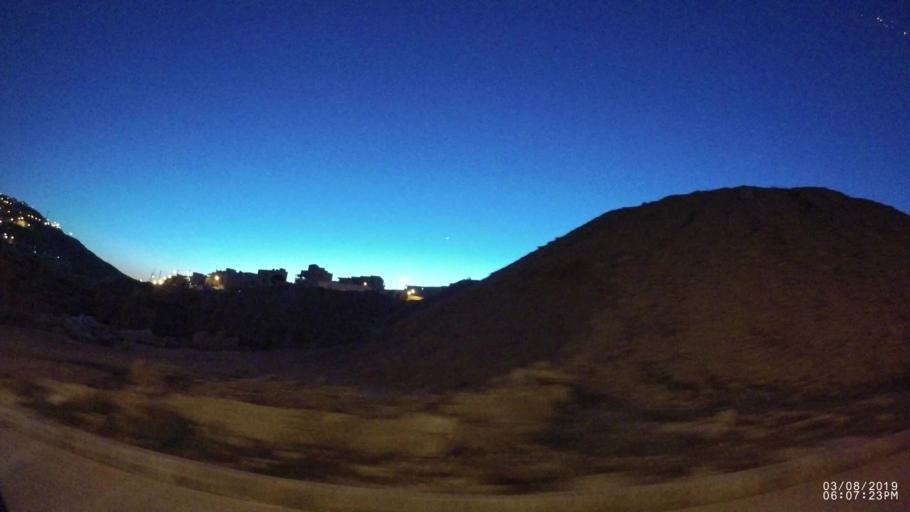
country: JO
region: Ma'an
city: Petra
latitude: 30.3300
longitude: 35.4771
